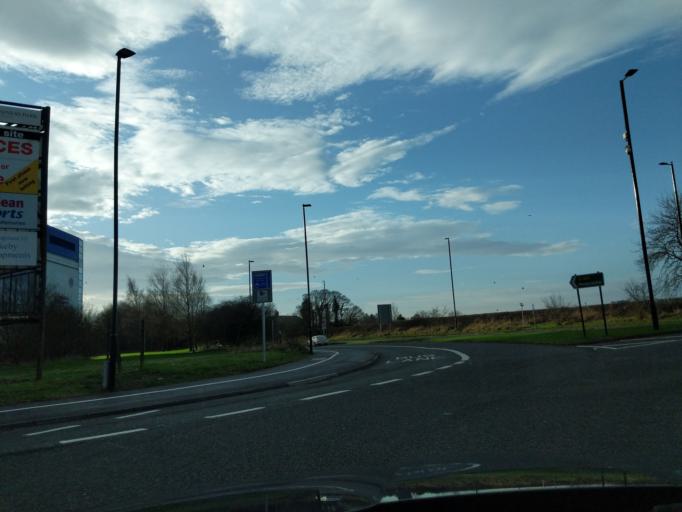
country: GB
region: England
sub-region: Newcastle upon Tyne
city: Gosforth
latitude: 55.0176
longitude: -1.5982
